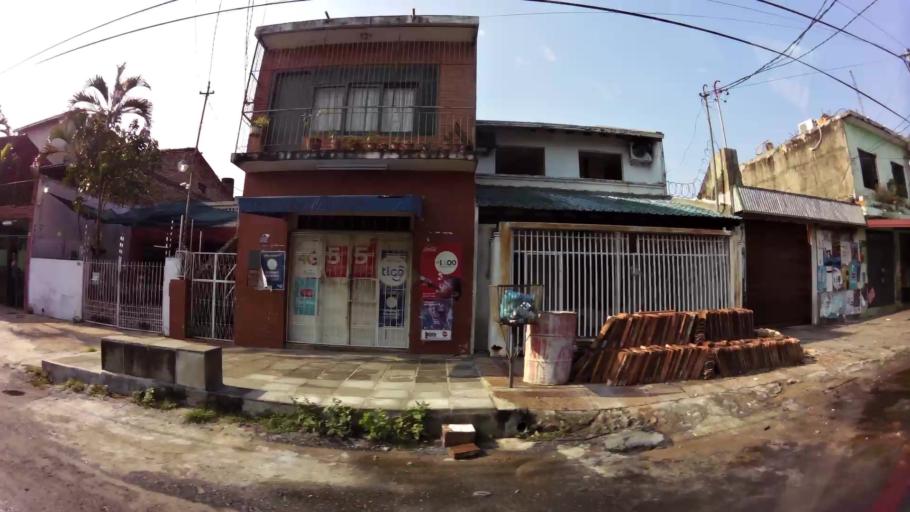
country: PY
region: Presidente Hayes
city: Nanawa
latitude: -25.2807
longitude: -57.6585
